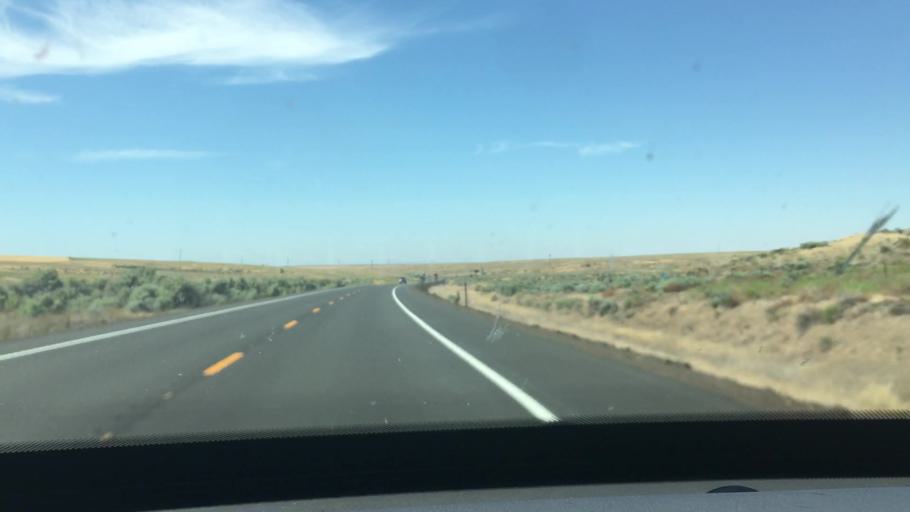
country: US
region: Oregon
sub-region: Sherman County
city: Moro
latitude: 45.2377
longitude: -120.7250
